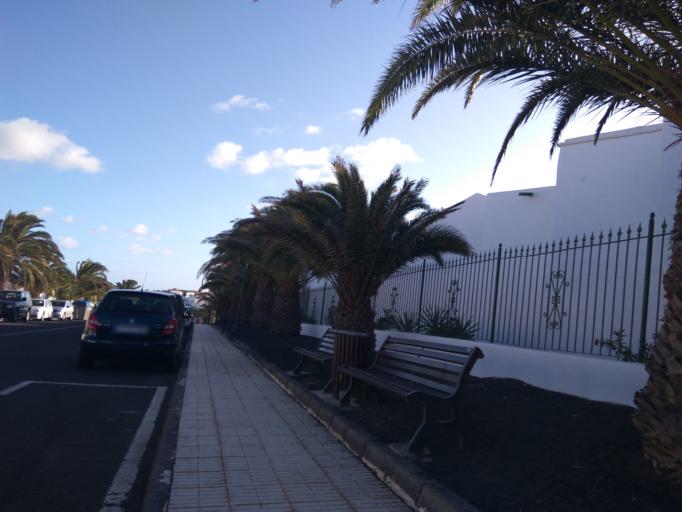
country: ES
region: Canary Islands
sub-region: Provincia de Las Palmas
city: Arrecife
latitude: 29.0065
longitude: -13.4907
